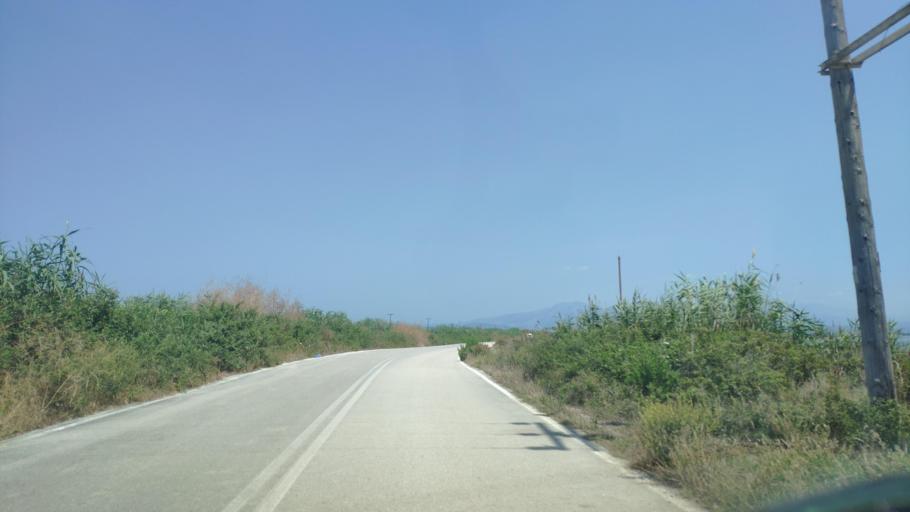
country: GR
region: Epirus
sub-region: Nomos Artas
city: Aneza
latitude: 39.0426
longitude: 20.8600
